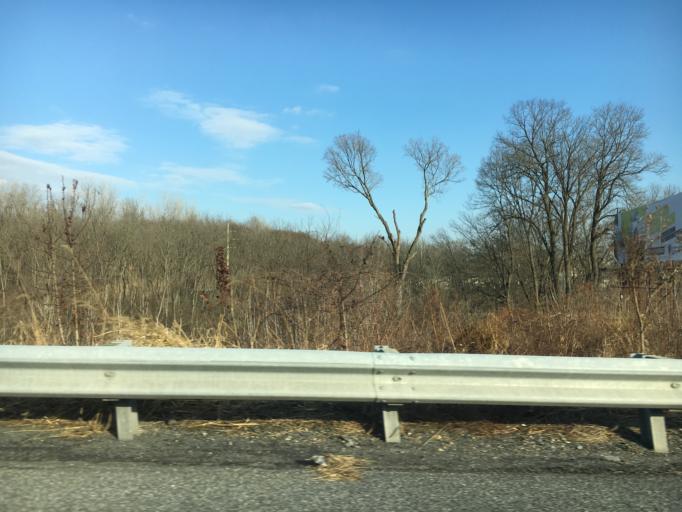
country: US
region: Pennsylvania
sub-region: Lehigh County
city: Stiles
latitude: 40.6699
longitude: -75.5147
